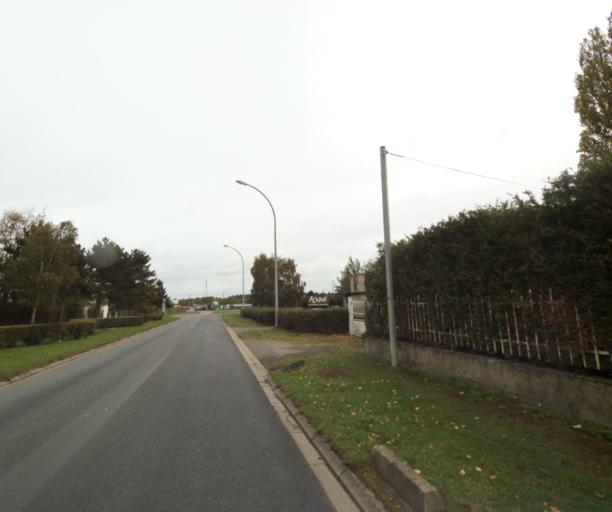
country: FR
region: Centre
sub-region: Departement d'Eure-et-Loir
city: Dreux
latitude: 48.7529
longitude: 1.3656
